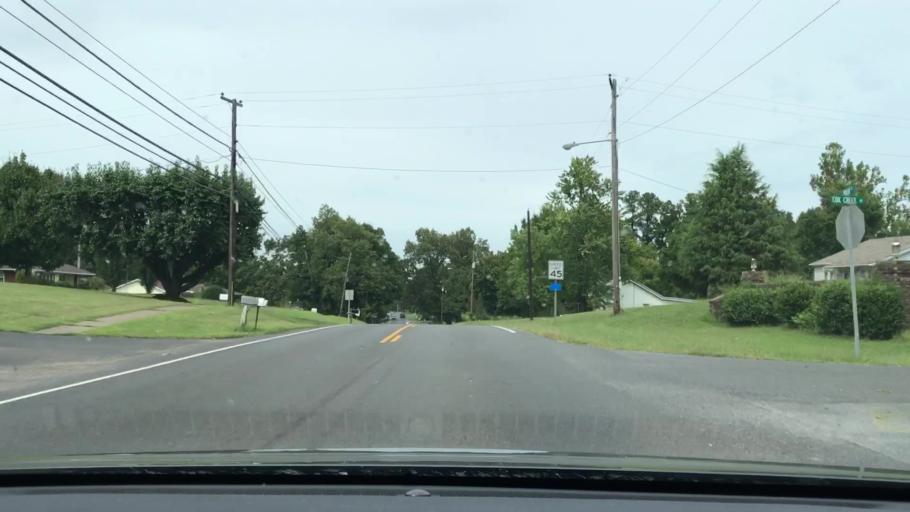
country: US
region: Kentucky
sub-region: Marshall County
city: Benton
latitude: 36.8422
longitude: -88.3498
